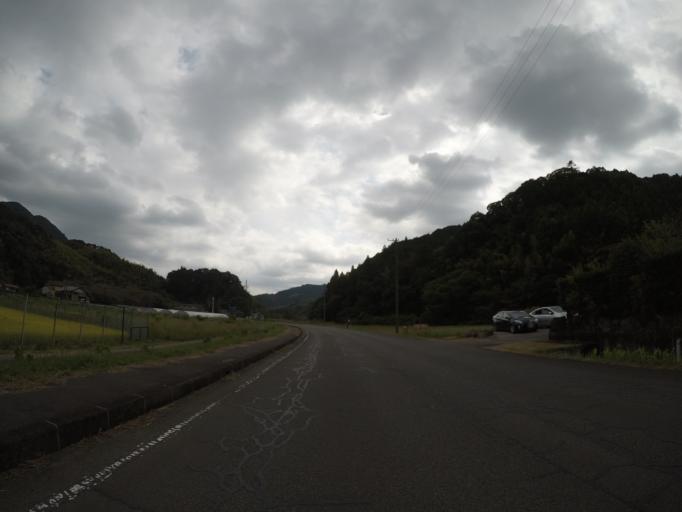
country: JP
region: Shizuoka
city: Fujieda
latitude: 34.9083
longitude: 138.1940
